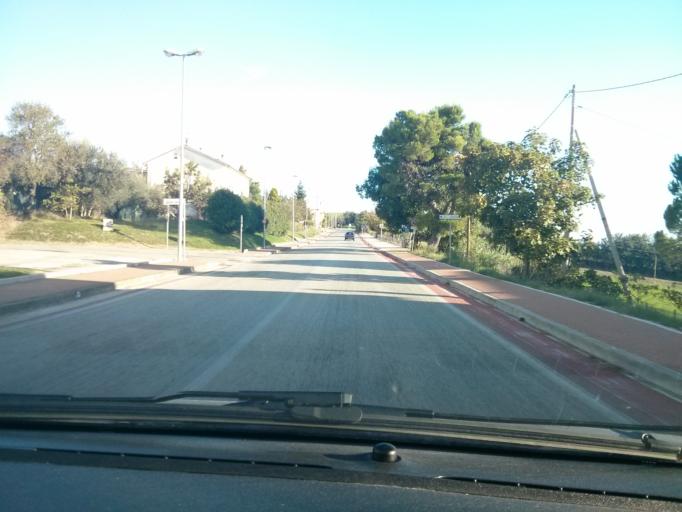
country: IT
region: The Marches
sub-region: Provincia di Pesaro e Urbino
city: Piagge
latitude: 43.7367
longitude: 12.9696
